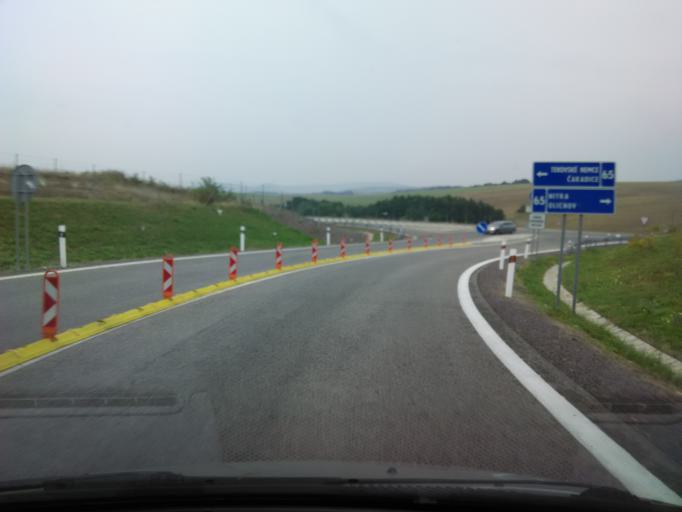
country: SK
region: Nitriansky
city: Tlmace
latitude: 48.3563
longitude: 18.4962
